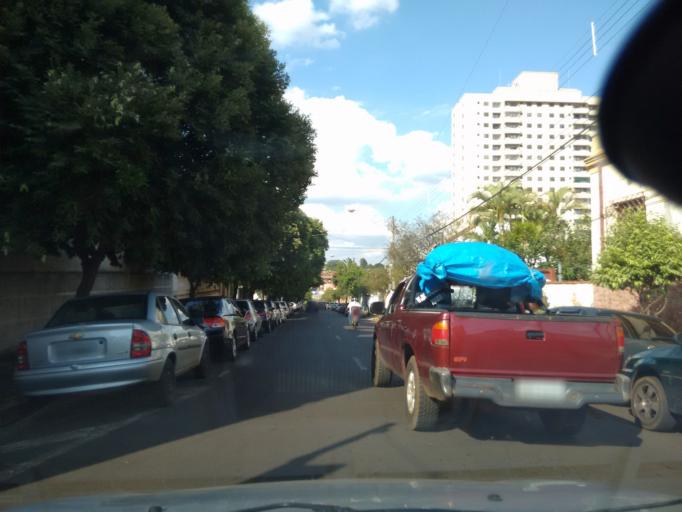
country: BR
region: Sao Paulo
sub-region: Araraquara
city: Araraquara
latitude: -21.7970
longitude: -48.1758
